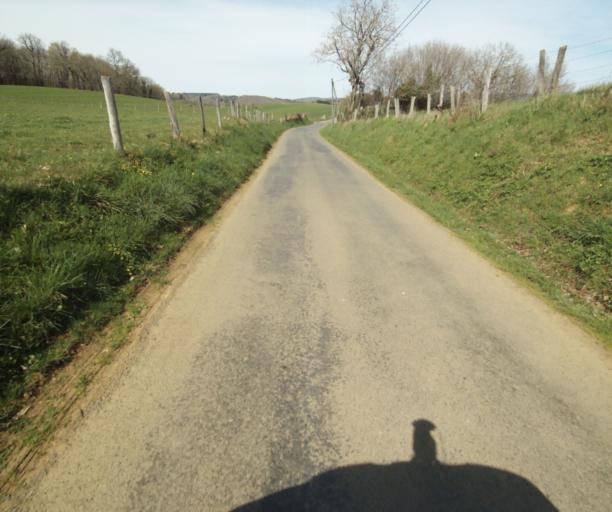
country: FR
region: Limousin
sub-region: Departement de la Correze
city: Naves
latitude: 45.3713
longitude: 1.7767
